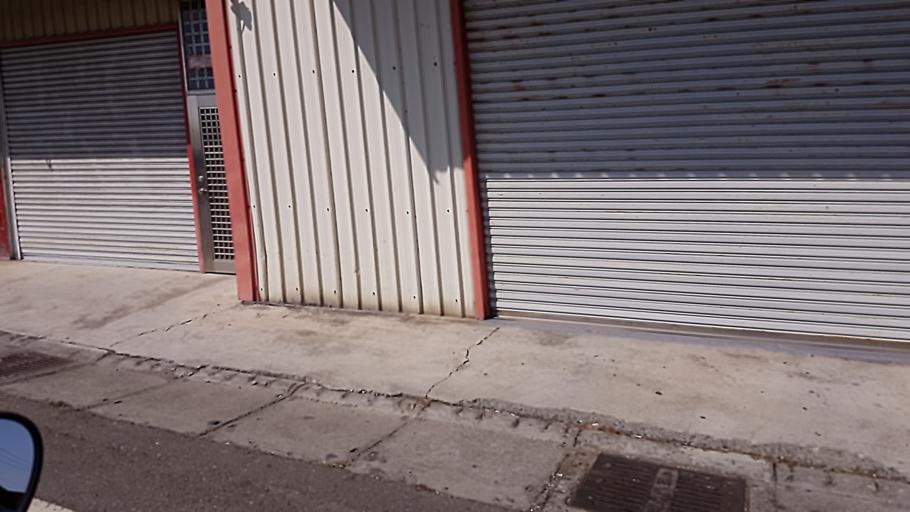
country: TW
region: Taiwan
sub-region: Changhua
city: Chang-hua
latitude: 24.0674
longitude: 120.4517
